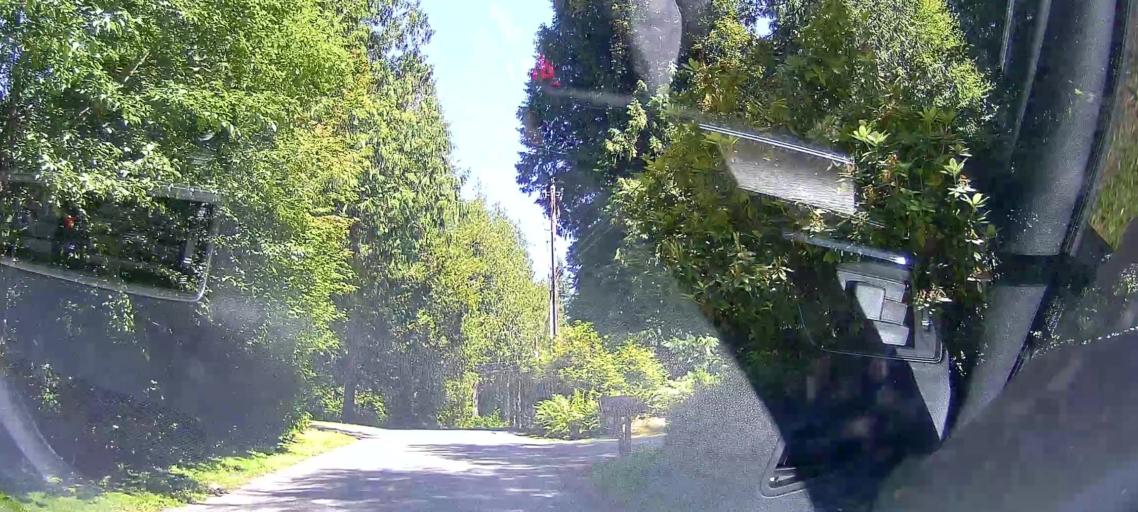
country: US
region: Washington
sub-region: Whatcom County
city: Sudden Valley
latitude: 48.6454
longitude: -122.3269
